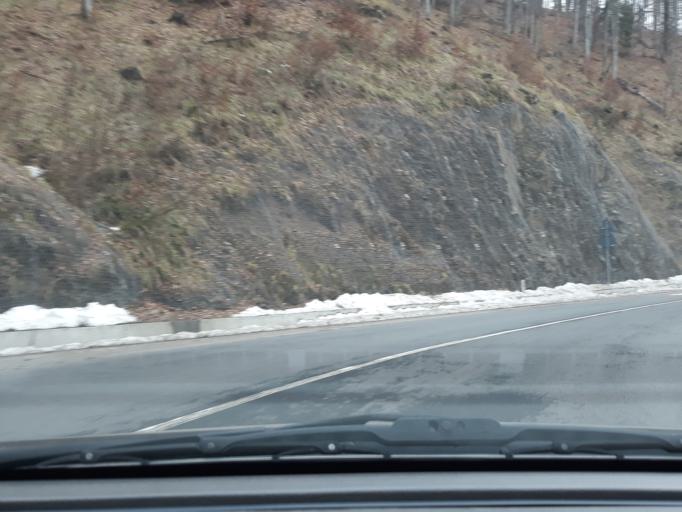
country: RO
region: Bihor
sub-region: Oras Alesd
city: Padurea Neagra
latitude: 47.1262
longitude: 22.4157
